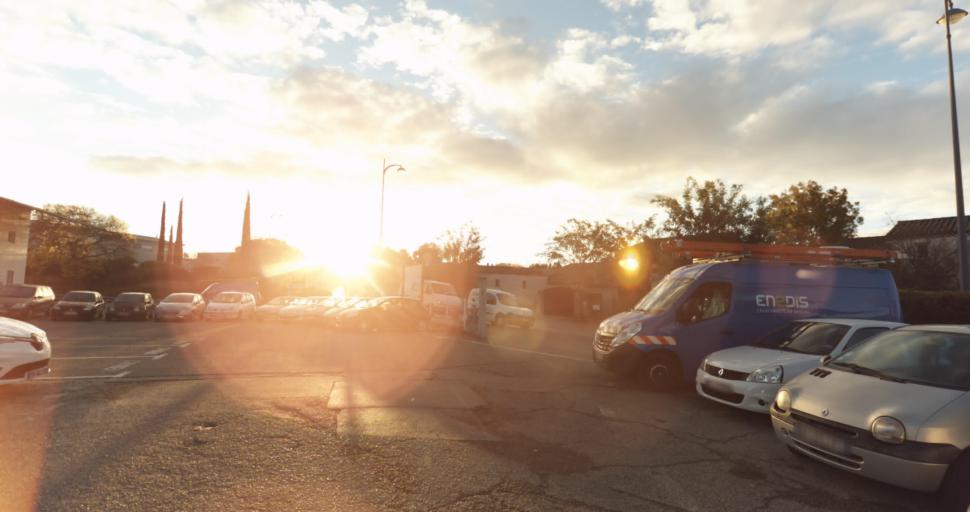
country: FR
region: Provence-Alpes-Cote d'Azur
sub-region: Departement des Bouches-du-Rhone
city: Venelles
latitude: 43.5808
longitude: 5.4720
